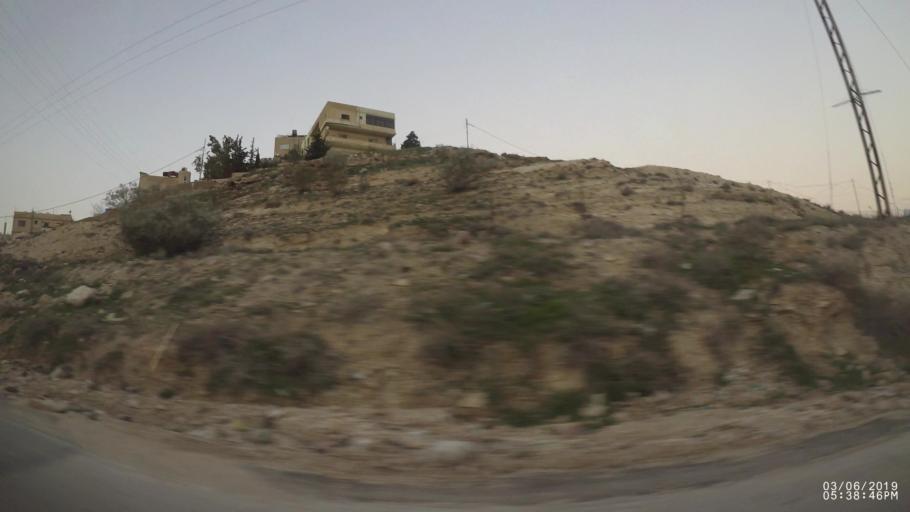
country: JO
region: Amman
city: Amman
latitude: 31.9938
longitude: 35.9769
